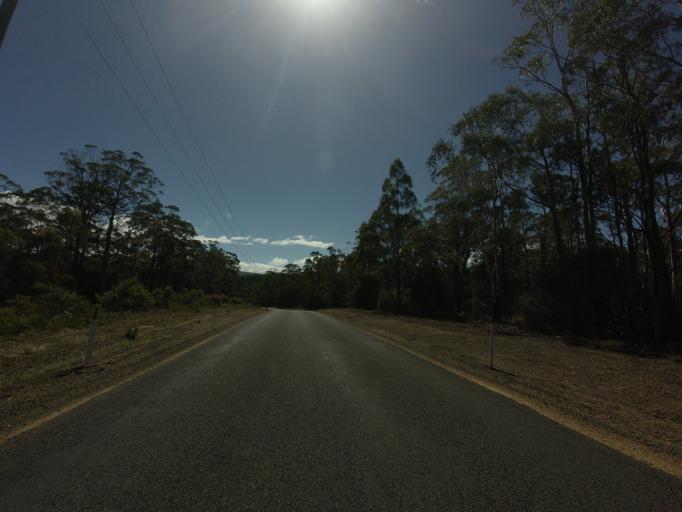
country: AU
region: Tasmania
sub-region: Break O'Day
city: St Helens
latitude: -41.5952
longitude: 148.2037
